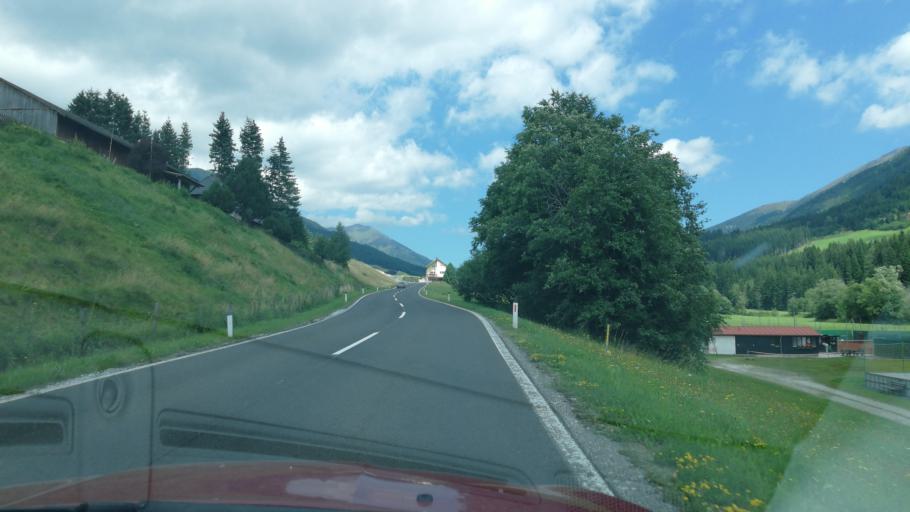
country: AT
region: Styria
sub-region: Politischer Bezirk Murtal
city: Sankt Johann am Tauern
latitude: 47.3598
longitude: 14.4680
